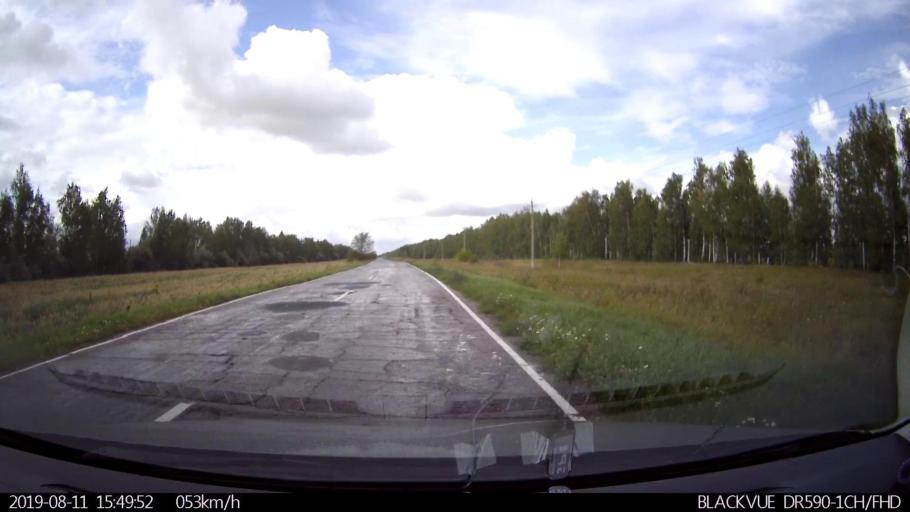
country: RU
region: Ulyanovsk
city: Ignatovka
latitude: 53.9077
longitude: 47.6555
